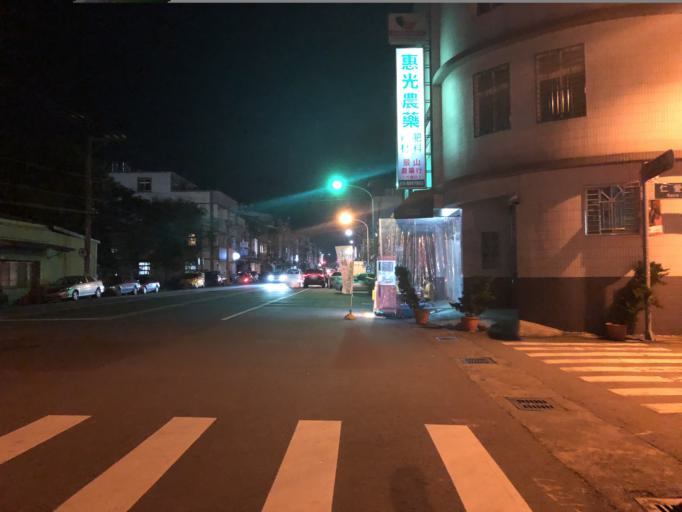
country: TW
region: Taiwan
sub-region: Hsinchu
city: Zhubei
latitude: 24.7331
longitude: 121.0928
